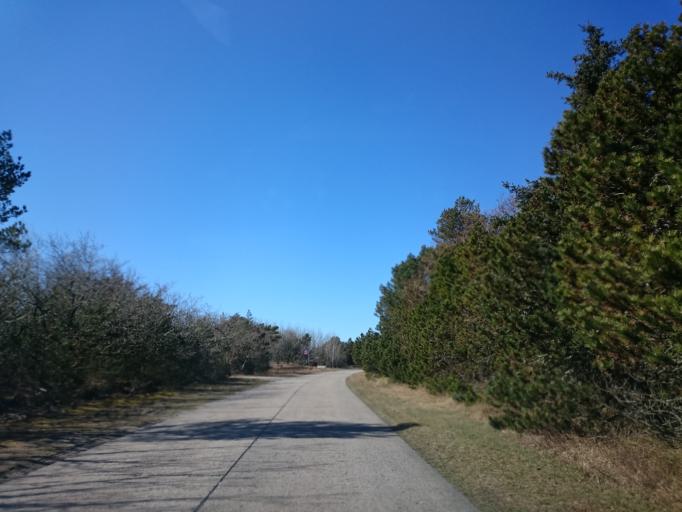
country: DK
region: North Denmark
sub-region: Frederikshavn Kommune
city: Skagen
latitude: 57.7204
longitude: 10.5344
